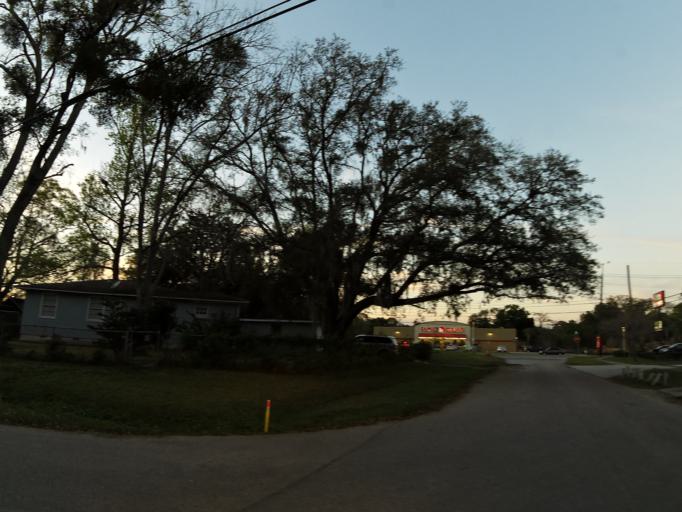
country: US
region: Florida
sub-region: Duval County
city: Jacksonville
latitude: 30.2900
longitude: -81.6223
